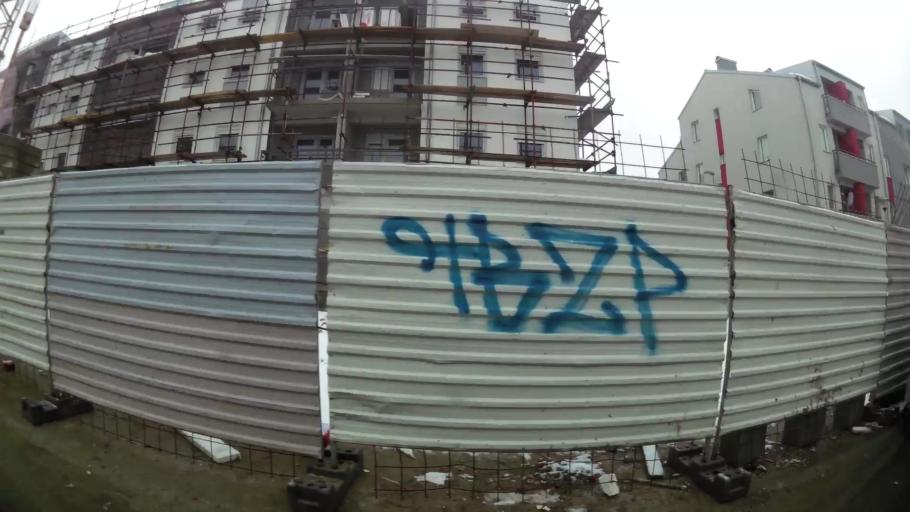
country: RS
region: Central Serbia
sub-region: Belgrade
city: Zemun
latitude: 44.8734
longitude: 20.3279
